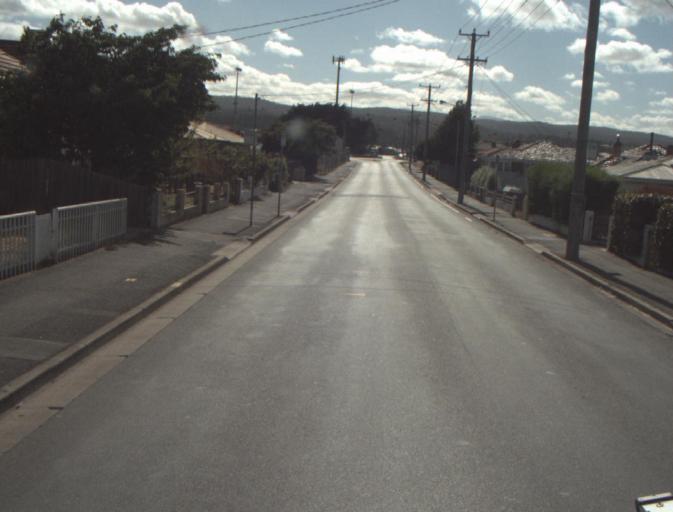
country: AU
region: Tasmania
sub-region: Launceston
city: Newnham
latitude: -41.4066
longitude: 147.1342
